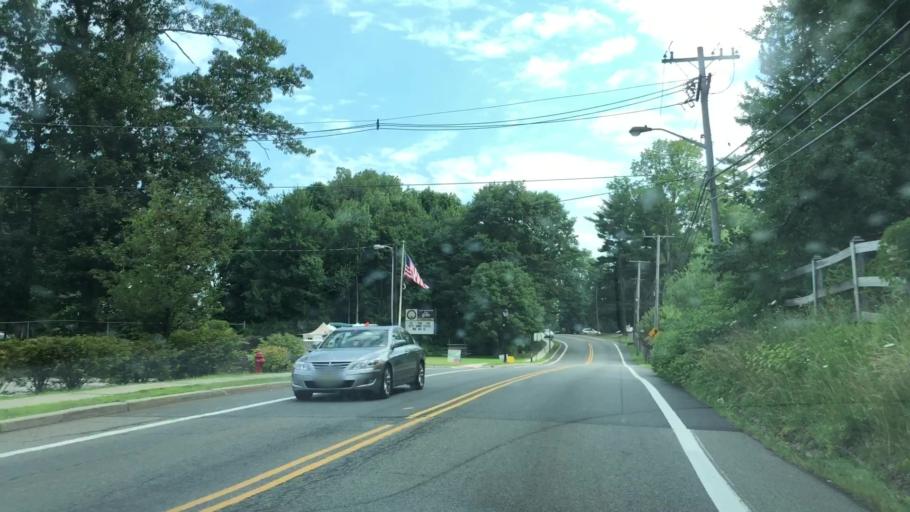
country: US
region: New Jersey
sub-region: Morris County
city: Mount Arlington
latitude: 40.9131
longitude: -74.6360
